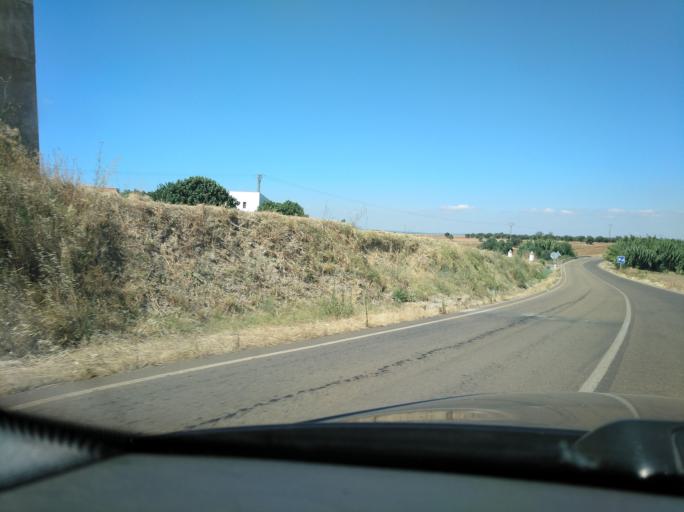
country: ES
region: Extremadura
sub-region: Provincia de Badajoz
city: Olivenza
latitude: 38.6902
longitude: -7.1119
